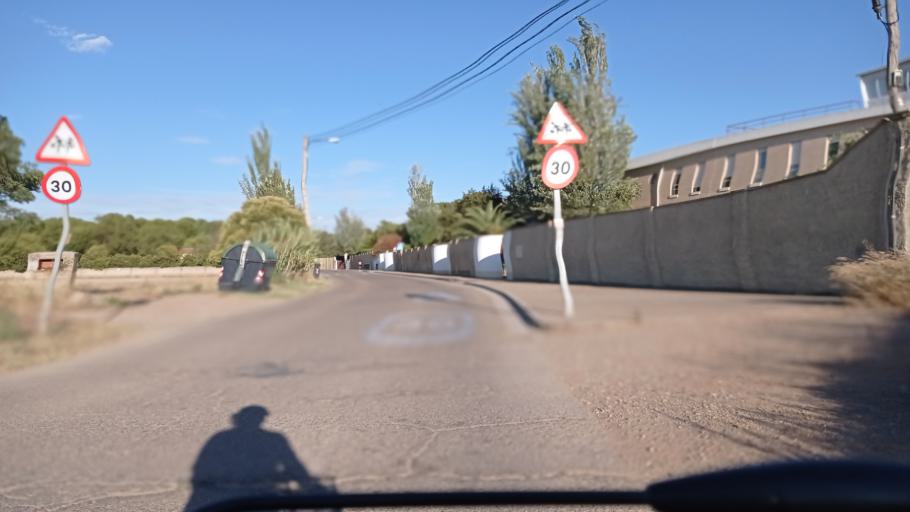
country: ES
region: Aragon
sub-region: Provincia de Zaragoza
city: Oliver-Valdefierro, Oliver, Valdefierro
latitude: 41.6754
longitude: -0.9610
